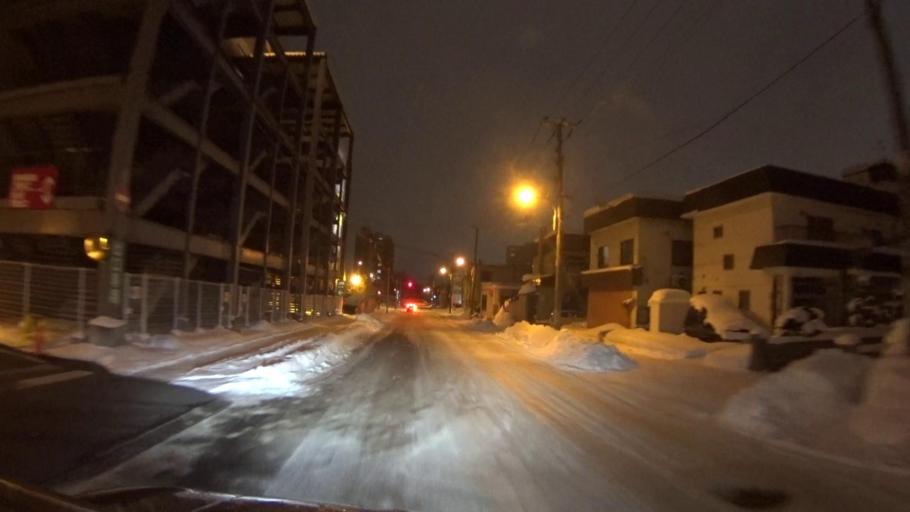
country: JP
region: Hokkaido
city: Sapporo
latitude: 43.0952
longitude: 141.2783
